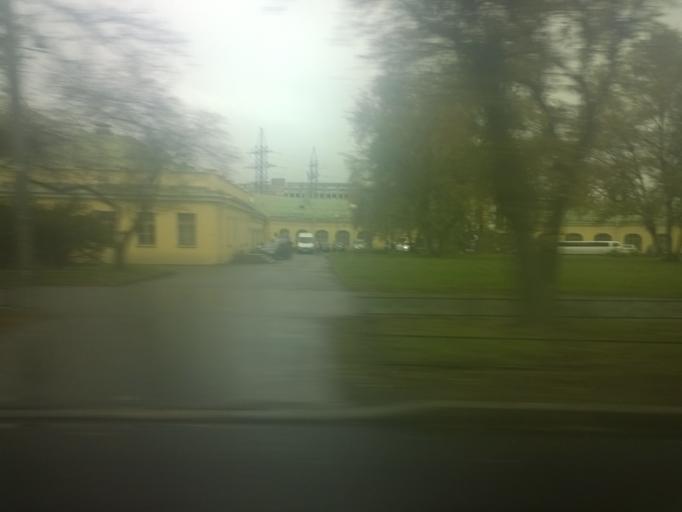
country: RU
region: St.-Petersburg
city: Avtovo
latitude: 59.8853
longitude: 30.2663
